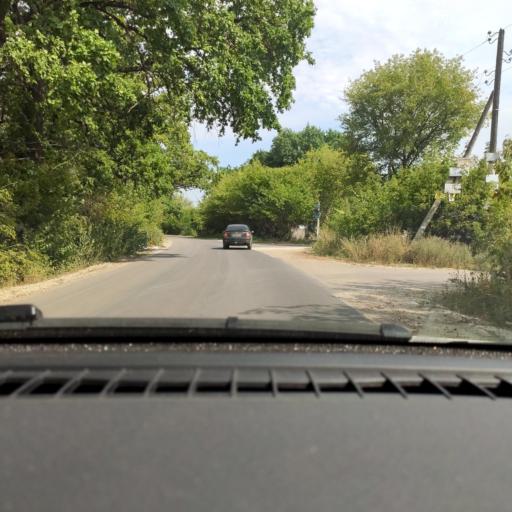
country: RU
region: Voronezj
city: Pridonskoy
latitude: 51.7402
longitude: 39.0699
